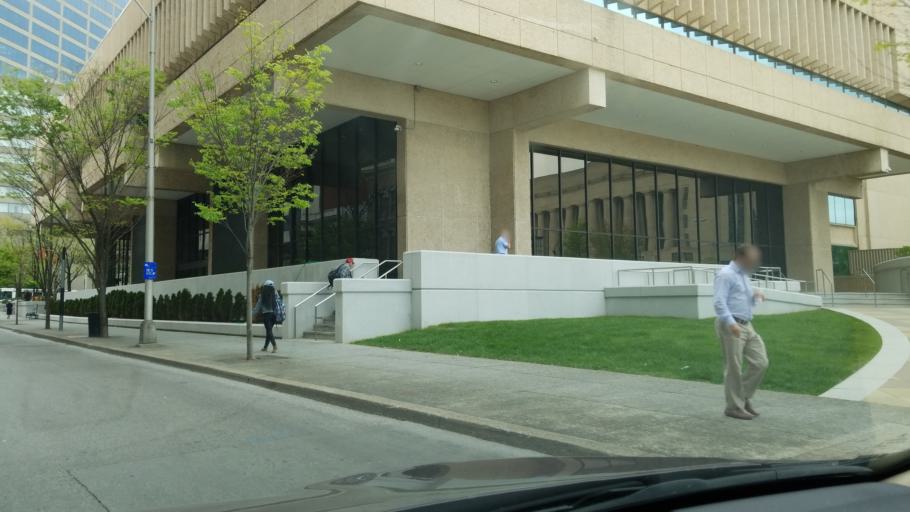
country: US
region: Tennessee
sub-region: Davidson County
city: Nashville
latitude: 36.1655
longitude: -86.7787
